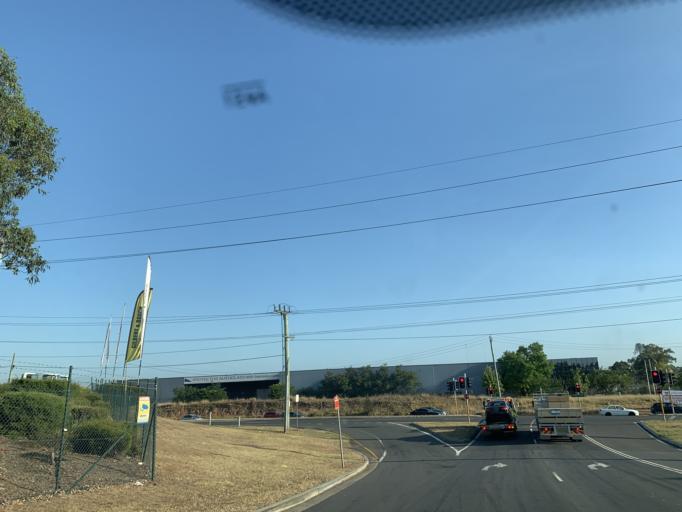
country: AU
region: New South Wales
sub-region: Blacktown
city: Doonside
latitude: -33.7961
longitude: 150.8885
